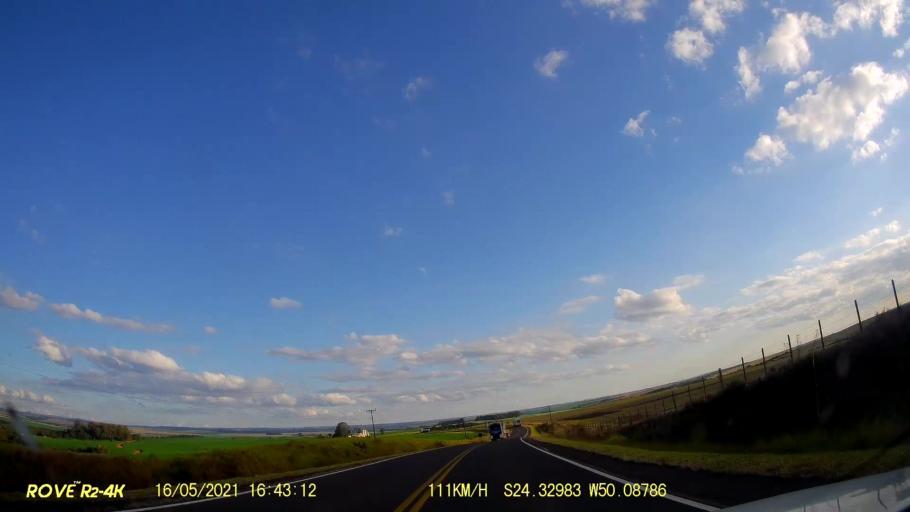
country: BR
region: Parana
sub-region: Pirai Do Sul
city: Pirai do Sul
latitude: -24.3305
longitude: -50.0879
